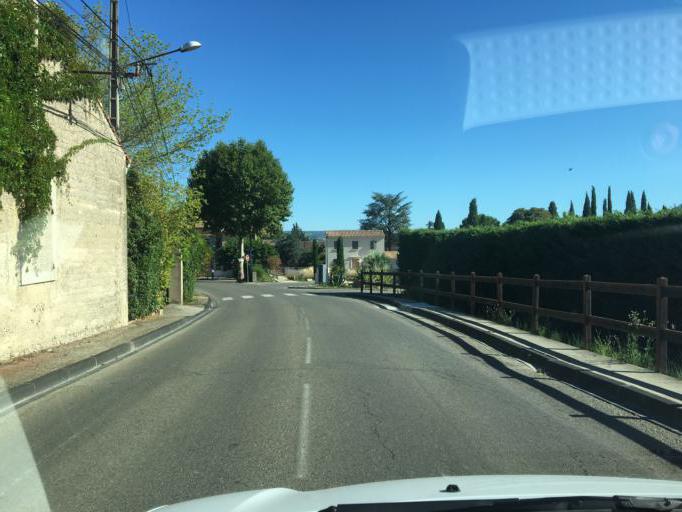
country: FR
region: Provence-Alpes-Cote d'Azur
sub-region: Departement du Vaucluse
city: Sablet
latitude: 44.1928
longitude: 5.0079
